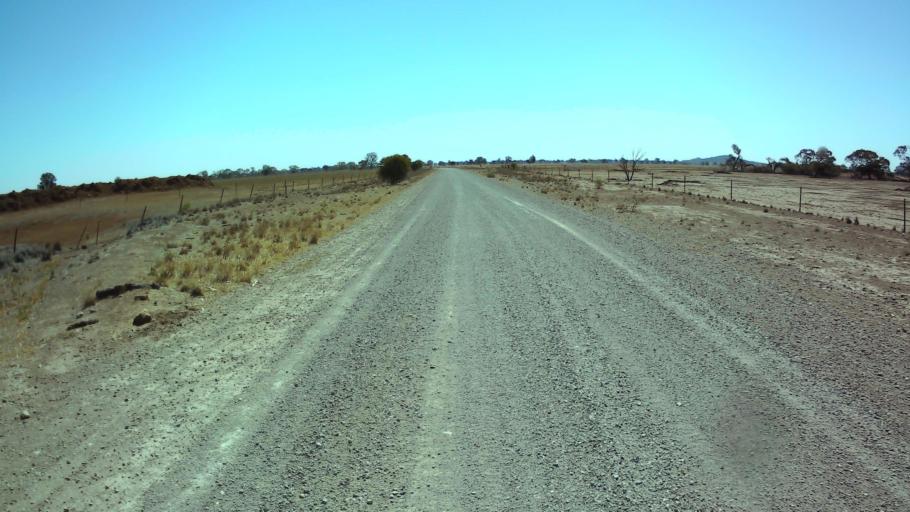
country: AU
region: New South Wales
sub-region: Forbes
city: Forbes
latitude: -33.7456
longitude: 147.7354
